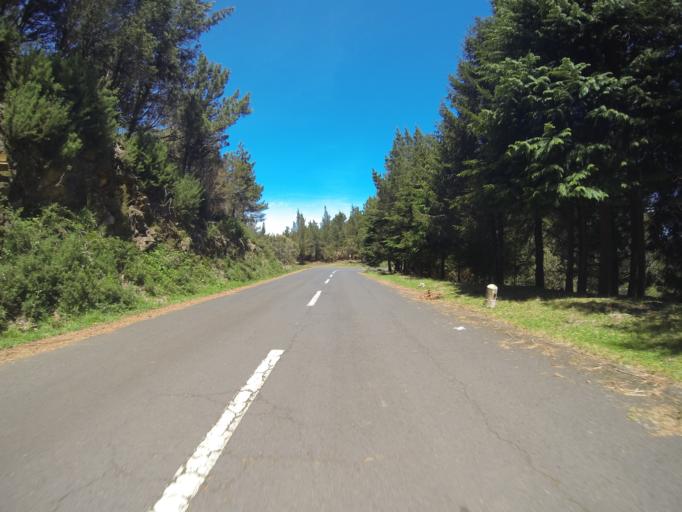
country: PT
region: Madeira
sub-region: Santa Cruz
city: Camacha
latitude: 32.7190
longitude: -16.8764
